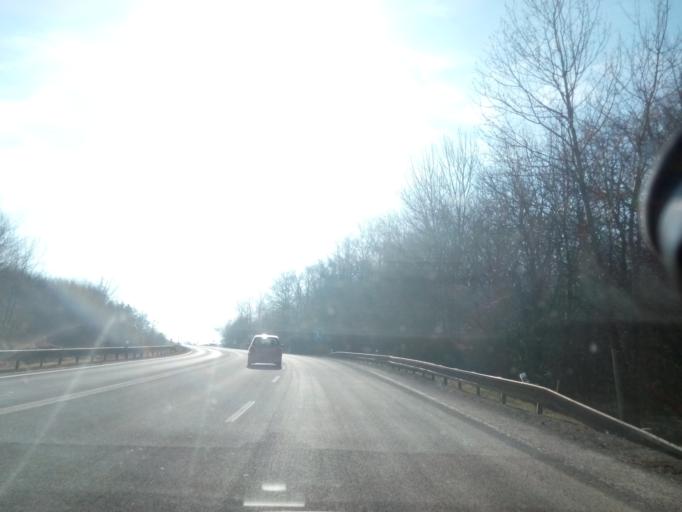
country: SK
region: Kosicky
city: Secovce
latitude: 48.7424
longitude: 21.5318
